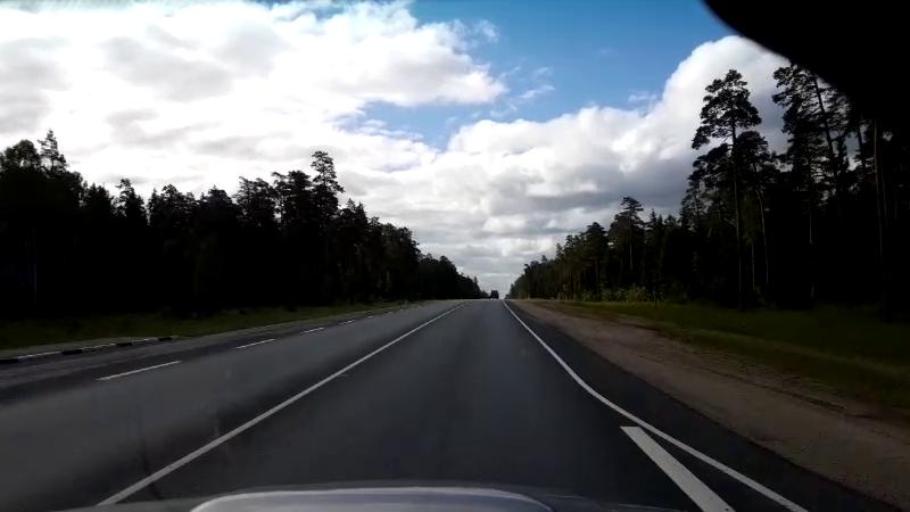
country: EE
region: Raplamaa
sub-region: Maerjamaa vald
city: Marjamaa
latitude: 59.0194
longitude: 24.4515
